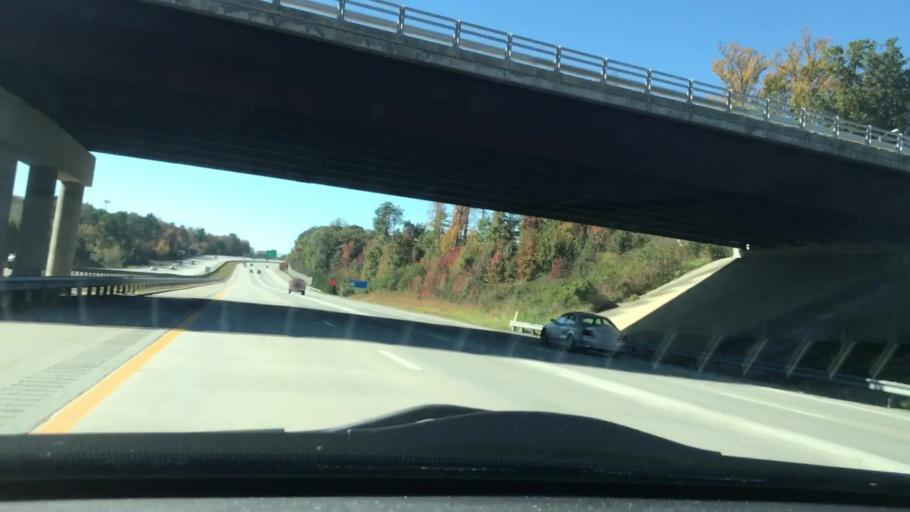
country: US
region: North Carolina
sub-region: Guilford County
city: Jamestown
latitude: 36.0454
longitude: -79.9023
